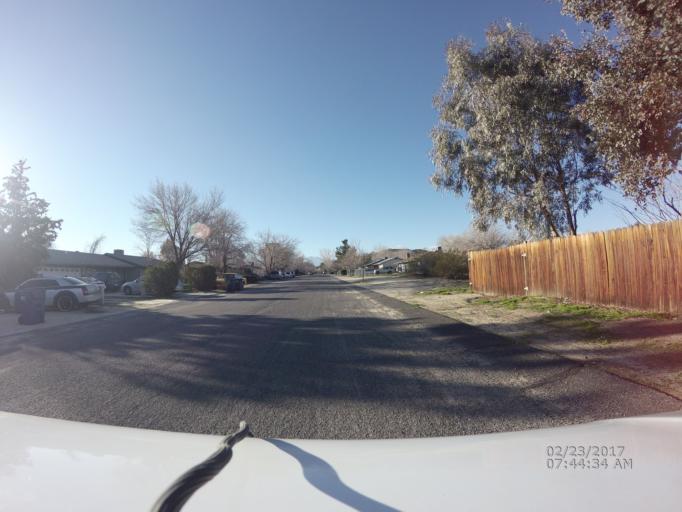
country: US
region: California
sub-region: Los Angeles County
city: Lake Los Angeles
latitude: 34.6157
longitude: -117.8124
